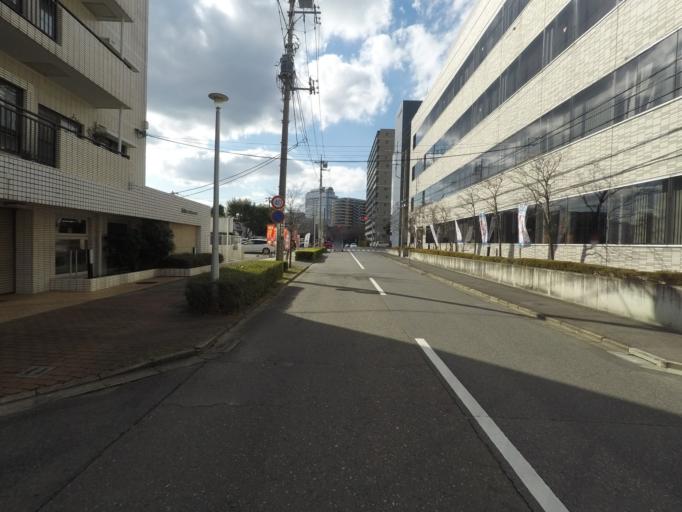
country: JP
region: Ibaraki
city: Naka
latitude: 36.0788
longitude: 140.1189
